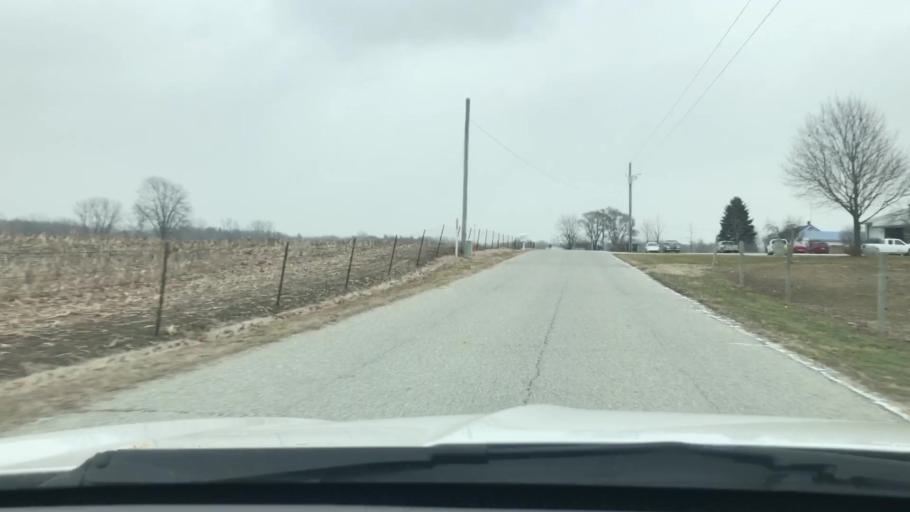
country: US
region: Indiana
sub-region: Fulton County
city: Akron
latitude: 41.0405
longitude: -86.0904
